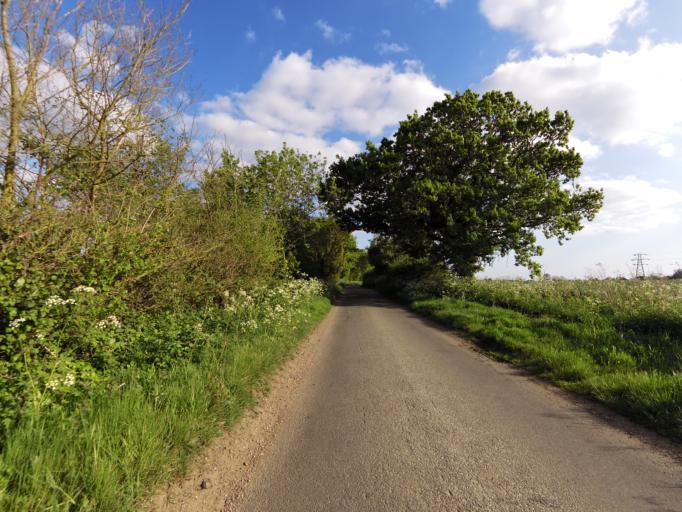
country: GB
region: England
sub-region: Suffolk
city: Beccles
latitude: 52.4200
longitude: 1.5054
